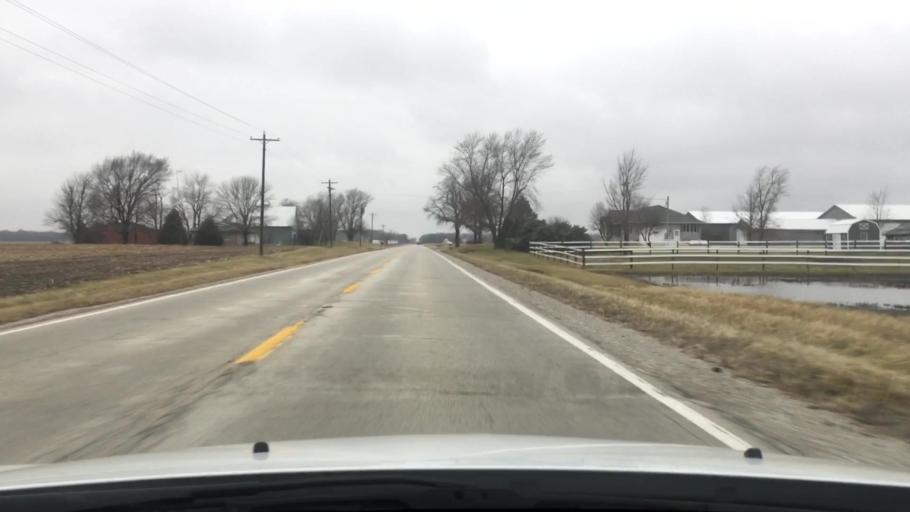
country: US
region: Illinois
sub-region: Iroquois County
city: Clifton
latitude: 40.8882
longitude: -87.8124
